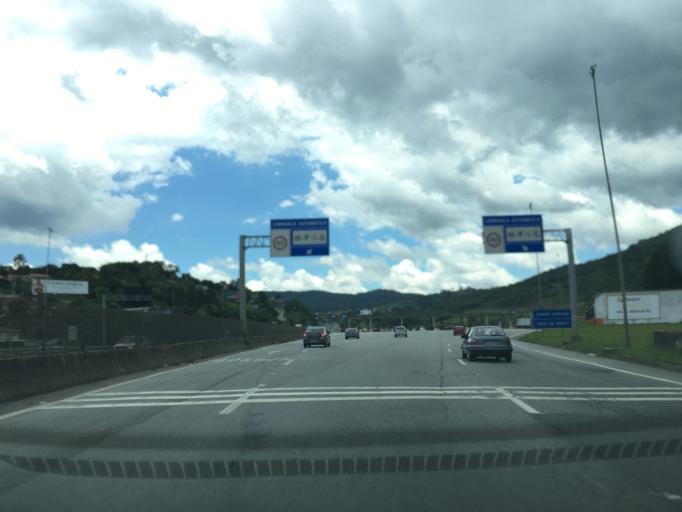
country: BR
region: Sao Paulo
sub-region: Mairipora
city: Mairipora
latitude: -23.3278
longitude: -46.5781
